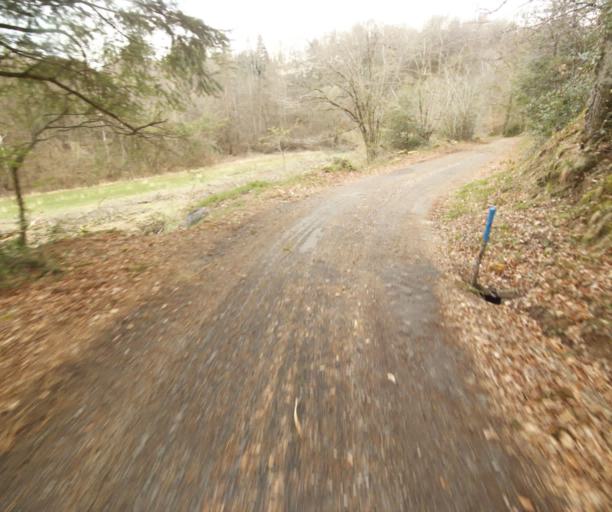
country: FR
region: Limousin
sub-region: Departement de la Correze
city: Saint-Privat
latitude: 45.2151
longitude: 1.9958
